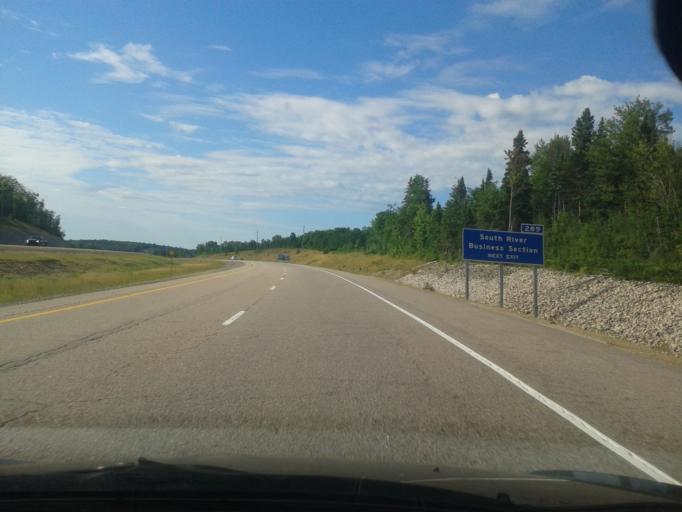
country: CA
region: Ontario
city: South River
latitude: 45.8871
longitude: -79.3806
